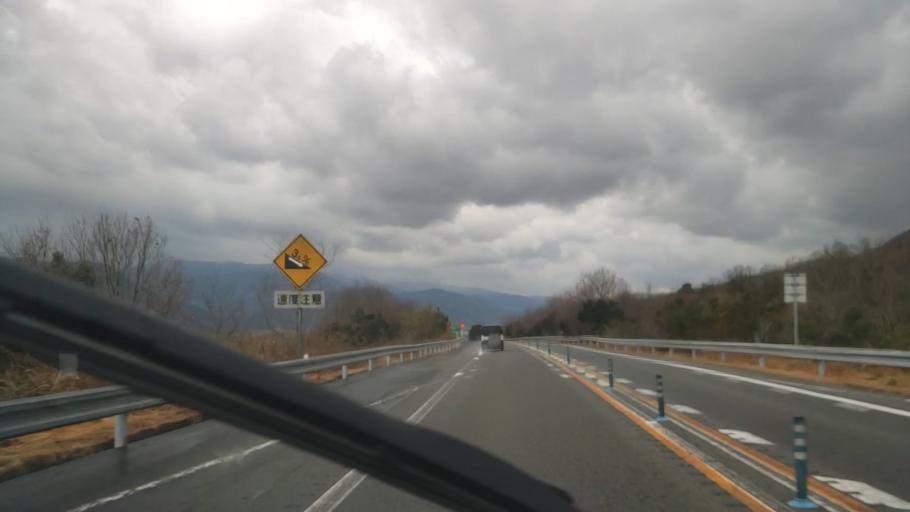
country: JP
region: Tokushima
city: Wakimachi
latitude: 34.0659
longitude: 134.0723
